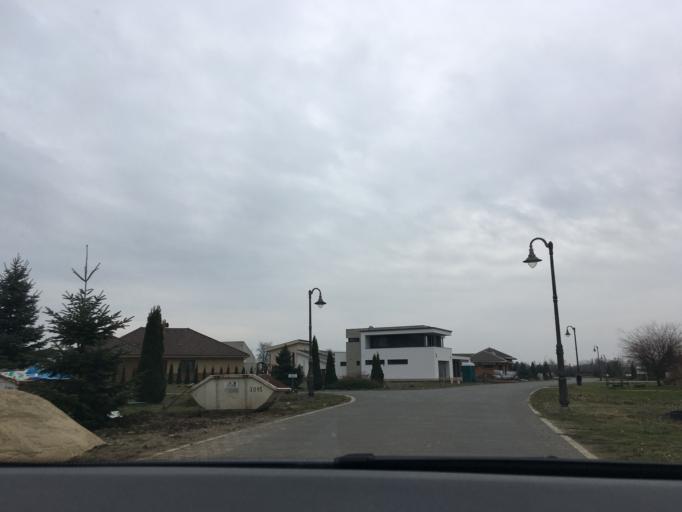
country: HU
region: Hajdu-Bihar
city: Debrecen
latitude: 47.5506
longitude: 21.6896
